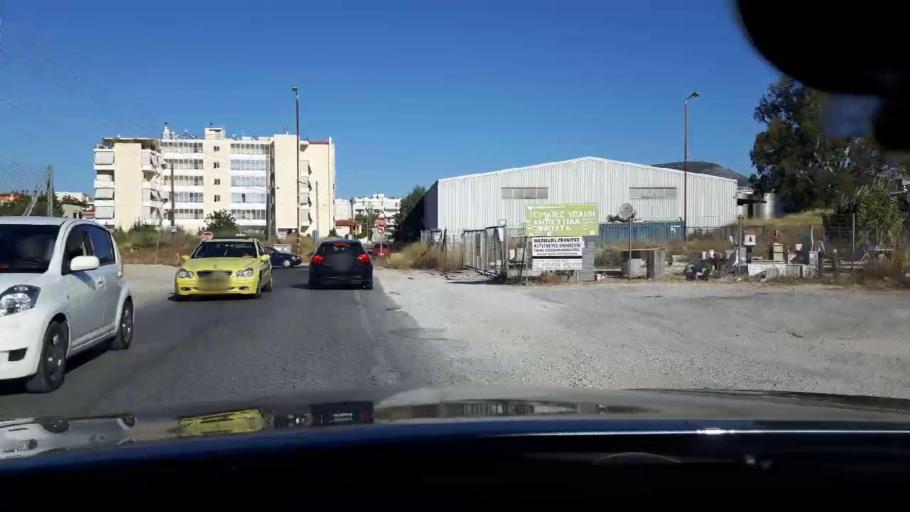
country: GR
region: Attica
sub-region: Nomarchia Anatolikis Attikis
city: Markopoulo
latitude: 37.8865
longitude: 23.9270
